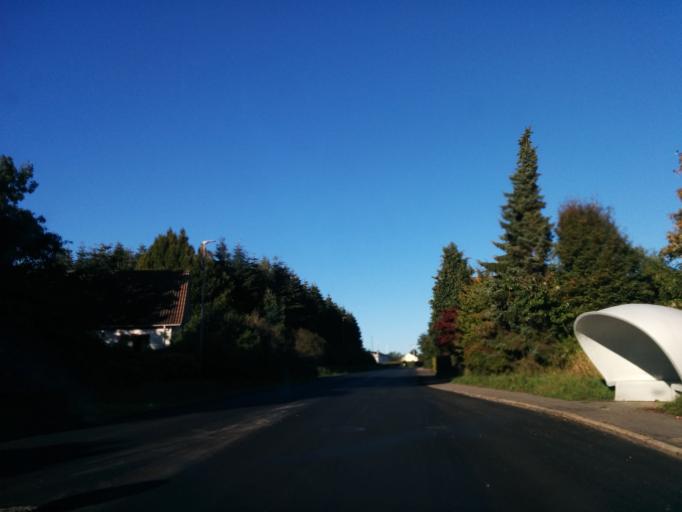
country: DK
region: South Denmark
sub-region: Kolding Kommune
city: Sonder Bjert
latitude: 55.4645
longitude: 9.5544
